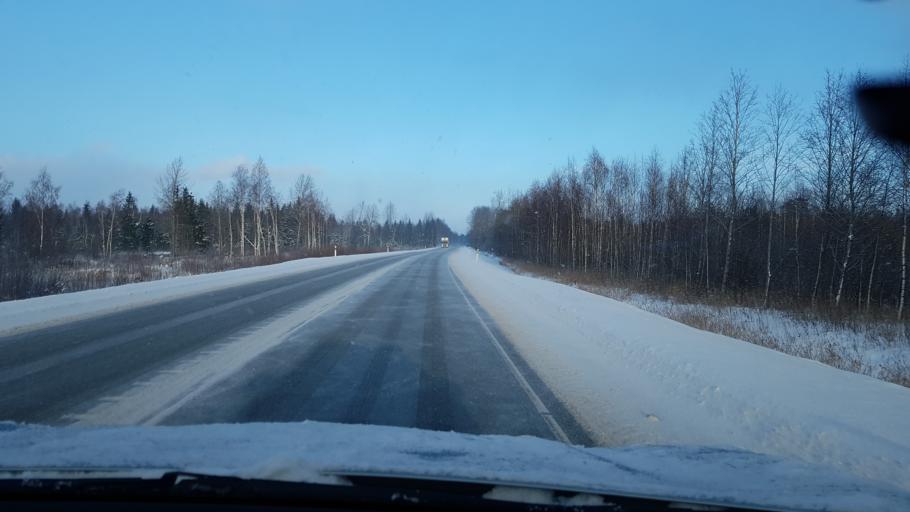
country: EE
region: Harju
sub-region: Nissi vald
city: Riisipere
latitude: 59.1606
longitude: 24.3436
